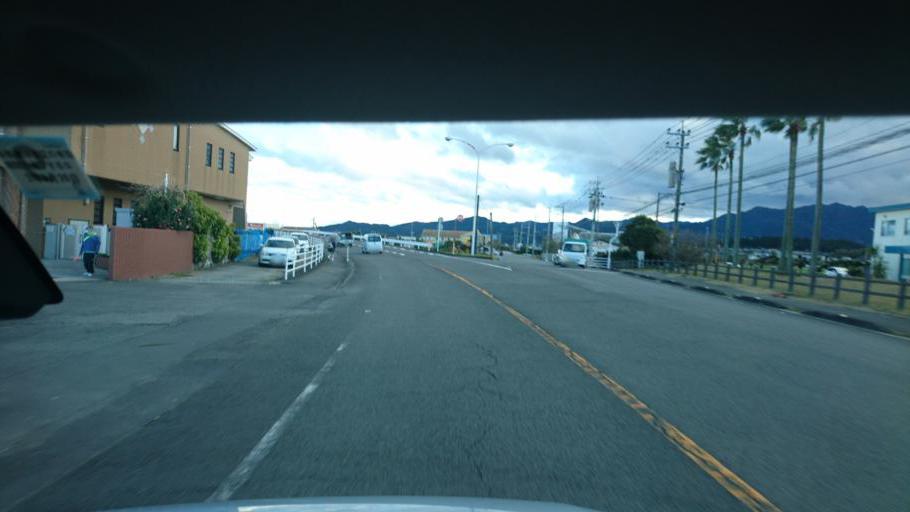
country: JP
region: Miyazaki
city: Miyazaki-shi
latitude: 31.8414
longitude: 131.4346
